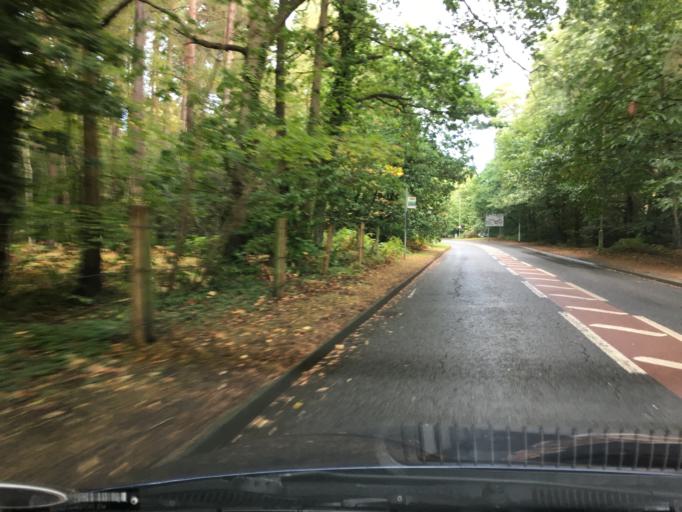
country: GB
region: England
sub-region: Bracknell Forest
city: Crowthorne
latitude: 51.3813
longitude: -0.8059
